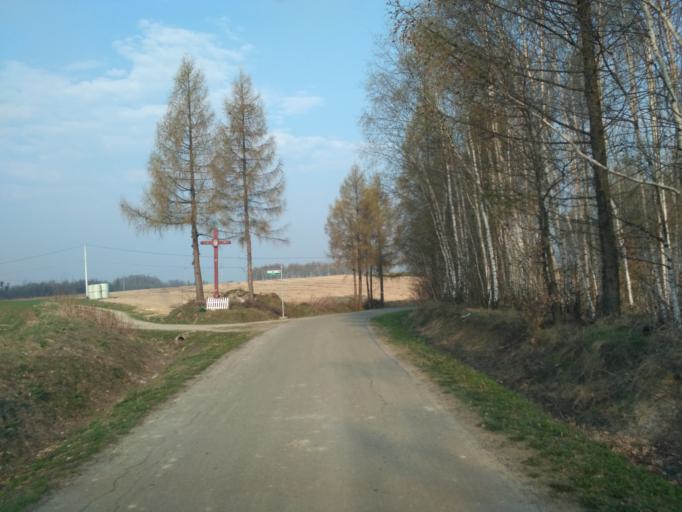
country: PL
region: Subcarpathian Voivodeship
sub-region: Powiat ropczycko-sedziszowski
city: Wielopole Skrzynskie
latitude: 49.9073
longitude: 21.6013
